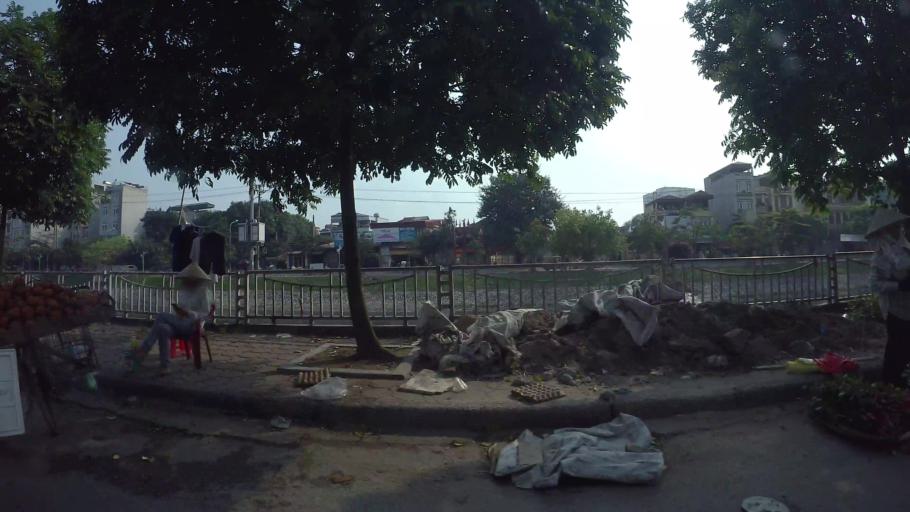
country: VN
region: Ha Noi
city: Thanh Xuan
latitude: 20.9820
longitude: 105.8171
